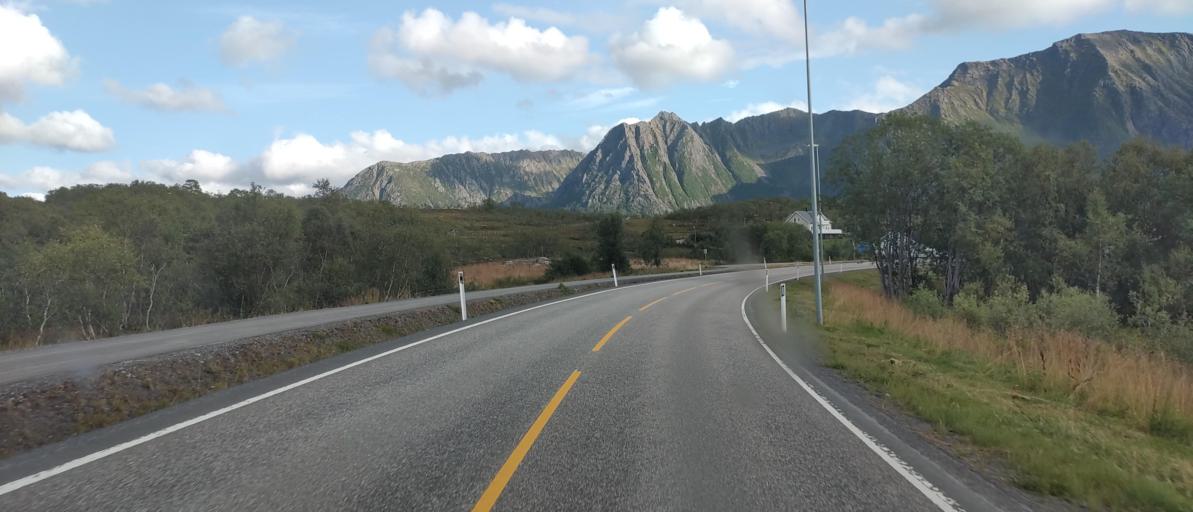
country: NO
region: Nordland
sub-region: Sortland
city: Sortland
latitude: 68.7422
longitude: 15.5159
